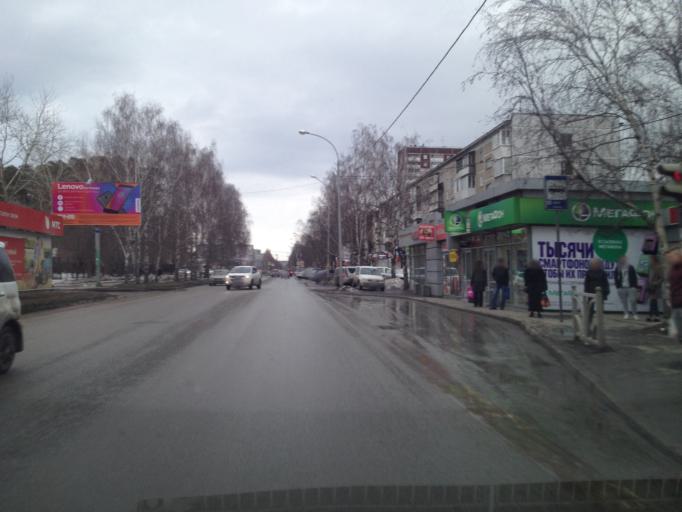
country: RU
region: Sverdlovsk
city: Sovkhoznyy
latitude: 56.8064
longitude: 60.5561
